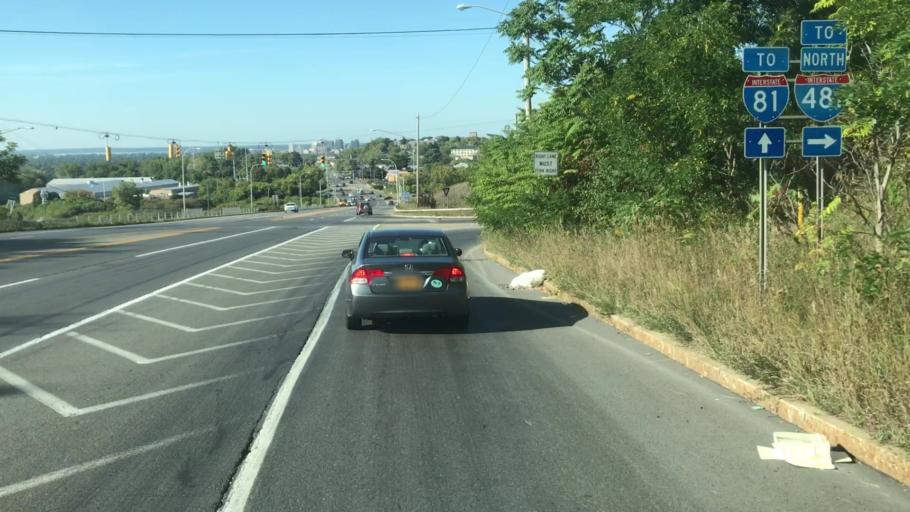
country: US
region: New York
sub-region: Onondaga County
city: Nedrow
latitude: 43.0054
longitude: -76.1311
